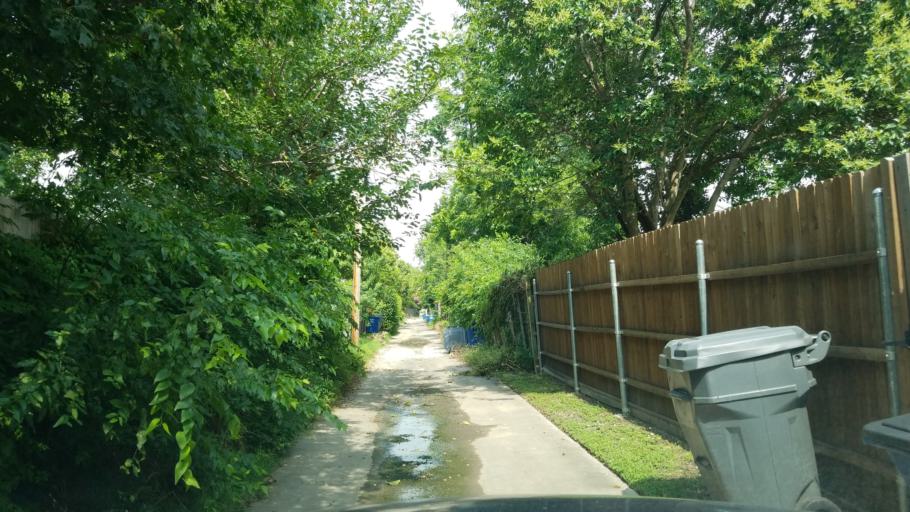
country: US
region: Texas
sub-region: Dallas County
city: Farmers Branch
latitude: 32.9008
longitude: -96.8766
